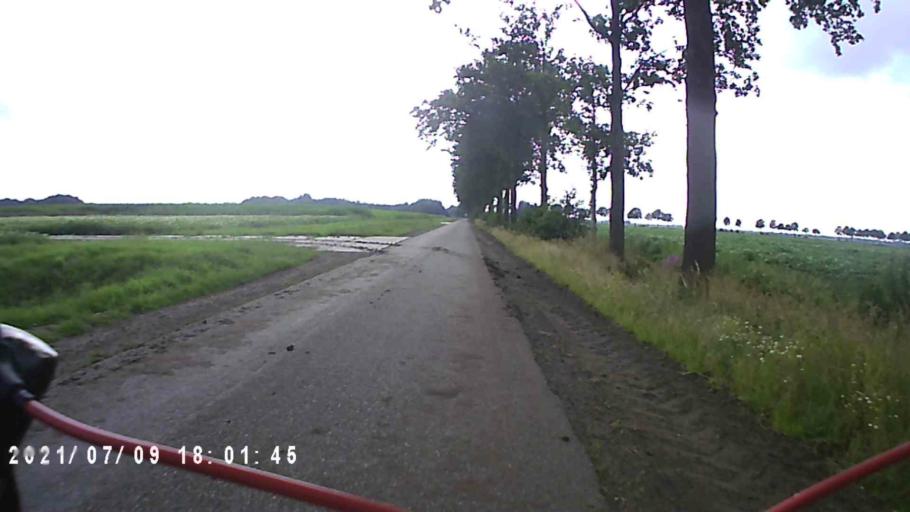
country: NL
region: Groningen
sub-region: Gemeente Pekela
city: Oude Pekela
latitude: 53.0690
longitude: 7.0560
